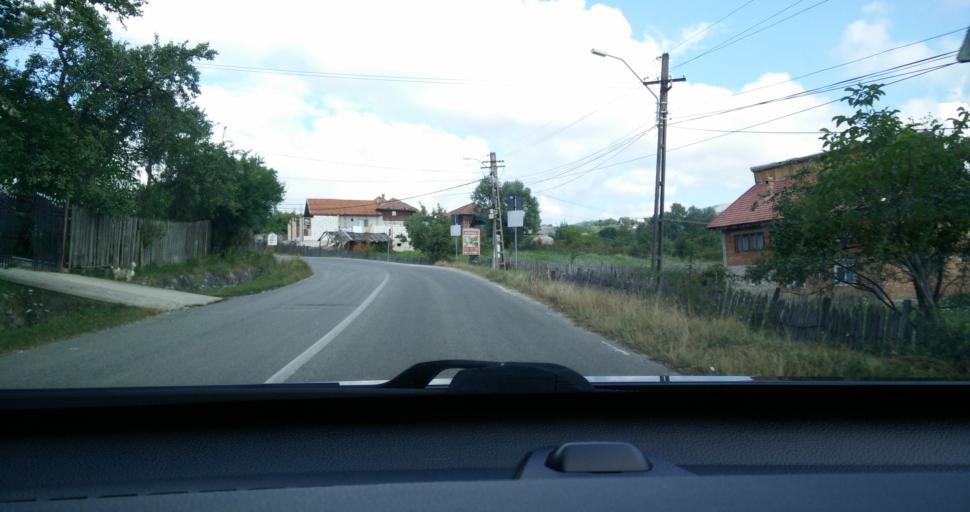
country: RO
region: Gorj
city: Novaci-Straini
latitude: 45.1767
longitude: 23.7056
